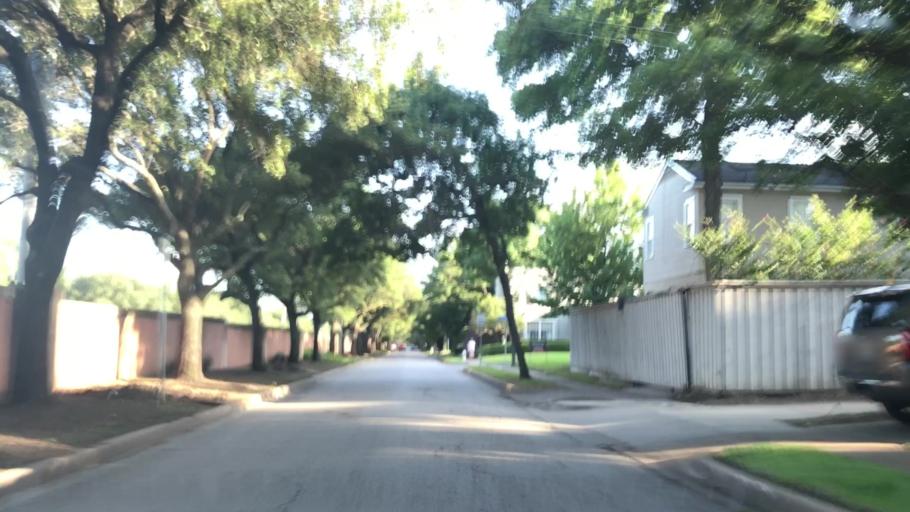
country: US
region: Texas
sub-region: Dallas County
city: University Park
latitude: 32.8346
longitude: -96.8155
